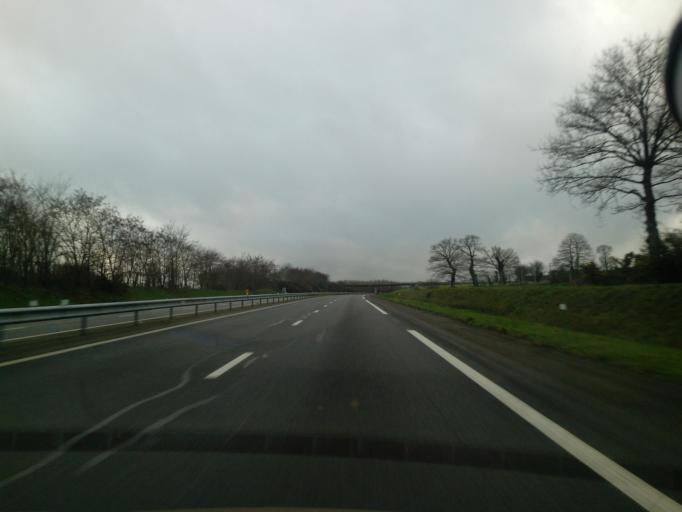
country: FR
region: Brittany
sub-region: Departement des Cotes-d'Armor
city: Plumaugat
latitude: 48.1942
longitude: -2.2774
